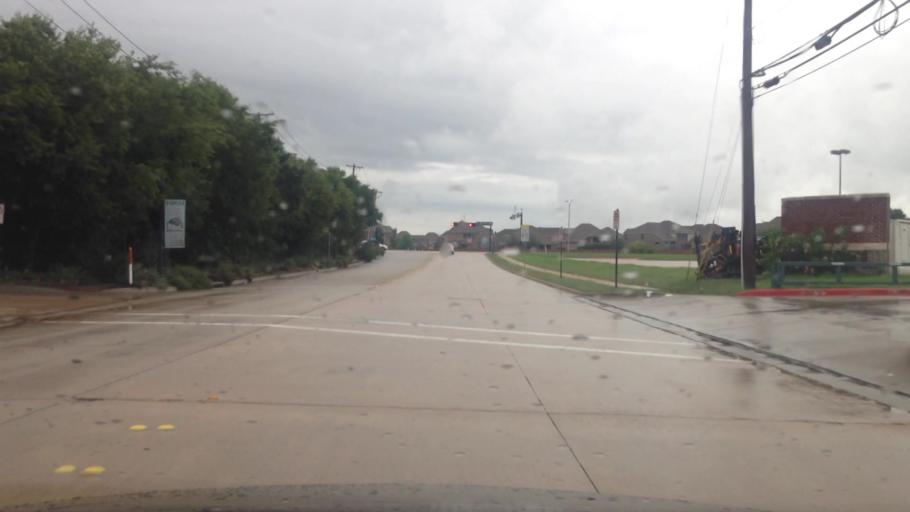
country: US
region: Texas
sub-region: Tarrant County
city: North Richland Hills
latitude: 32.8606
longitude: -97.1951
